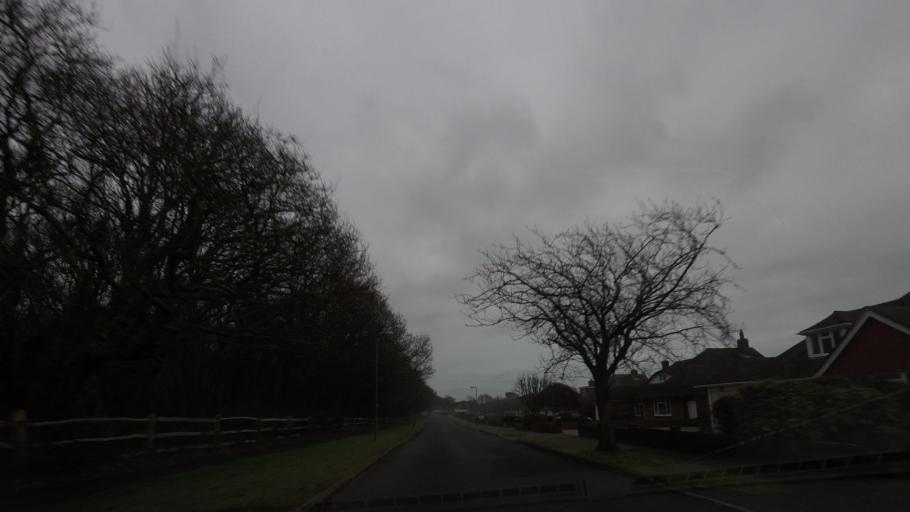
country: GB
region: England
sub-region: East Sussex
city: Bexhill-on-Sea
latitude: 50.8361
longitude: 0.4357
